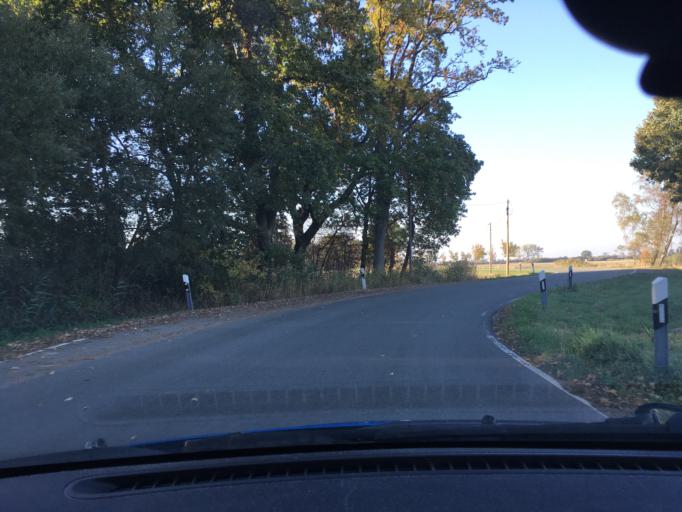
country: DE
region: Lower Saxony
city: Hitzacker
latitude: 53.1951
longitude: 10.9991
